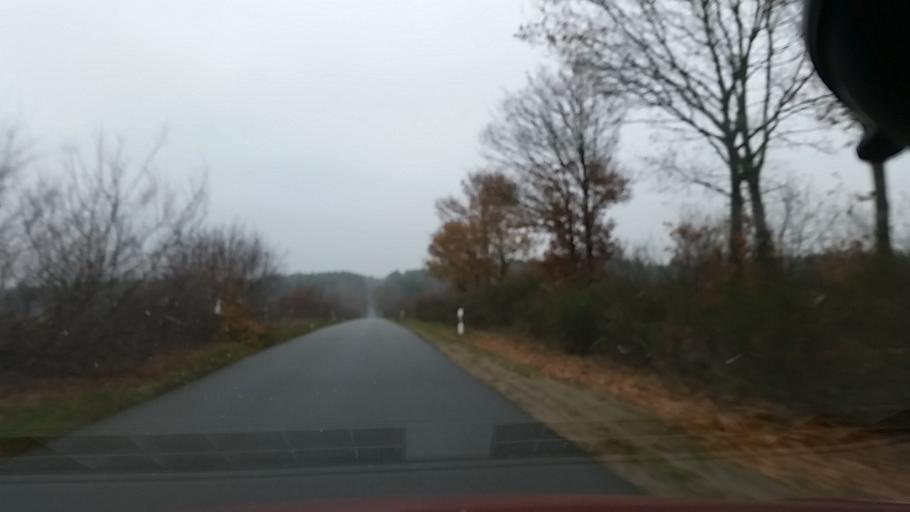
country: DE
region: Lower Saxony
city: Stadensen
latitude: 52.8143
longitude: 10.5469
